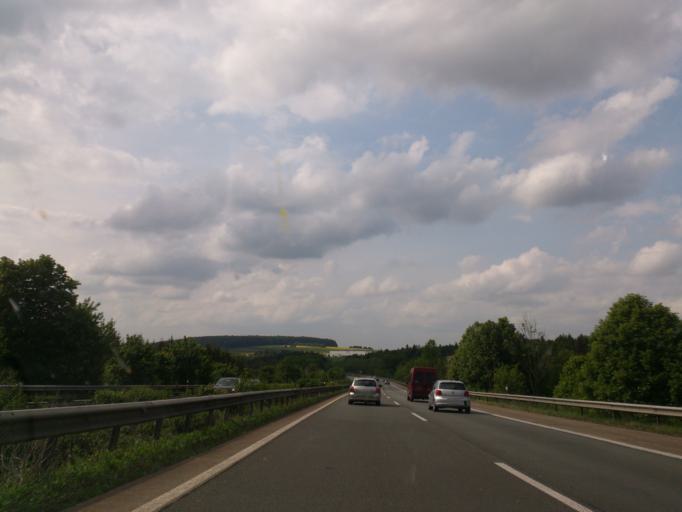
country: DE
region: Hesse
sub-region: Regierungsbezirk Kassel
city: Breuna
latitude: 51.3895
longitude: 9.2174
